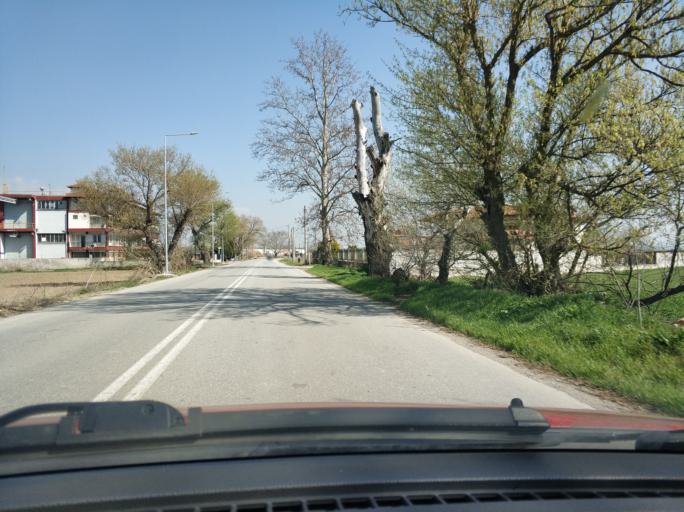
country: GR
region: Central Macedonia
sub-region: Nomos Thessalonikis
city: Lagyna
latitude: 40.7315
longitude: 23.0151
